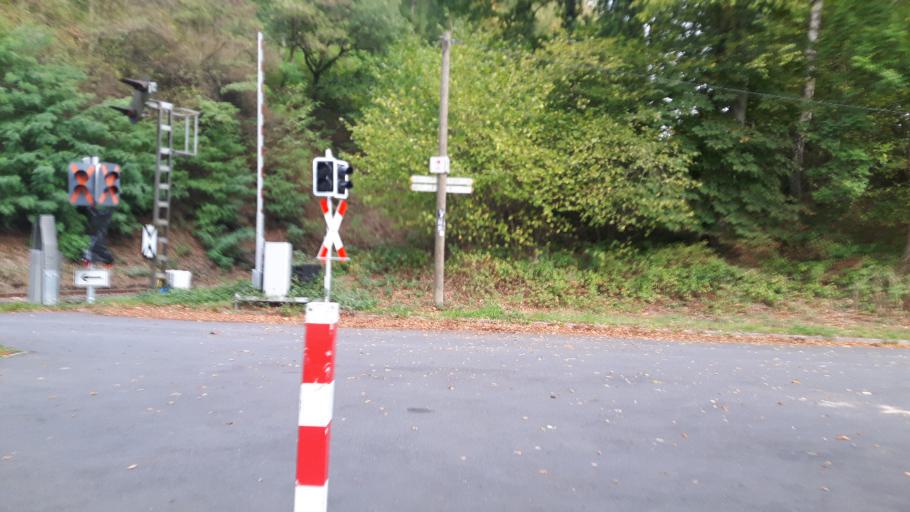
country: DE
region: North Rhine-Westphalia
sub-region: Regierungsbezirk Koln
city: Eitorf
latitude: 50.7698
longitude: 7.3866
